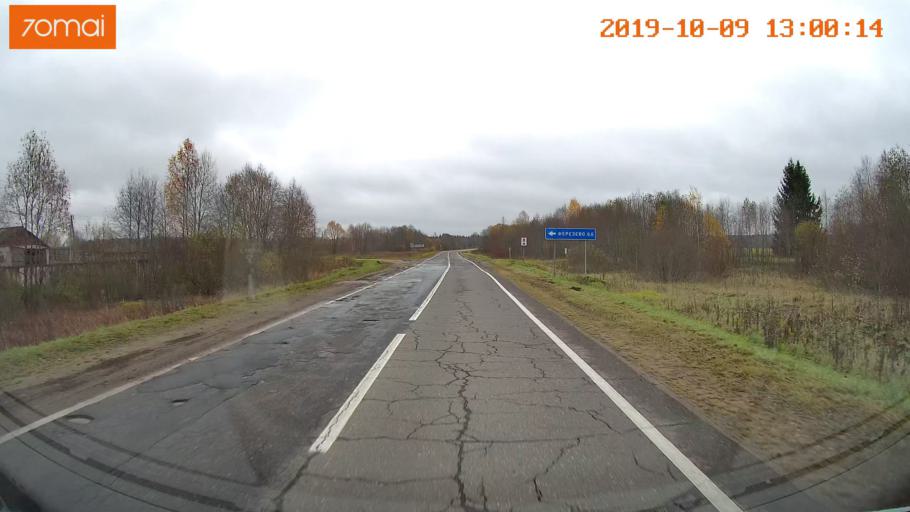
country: RU
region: Jaroslavl
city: Prechistoye
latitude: 58.3789
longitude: 40.4773
